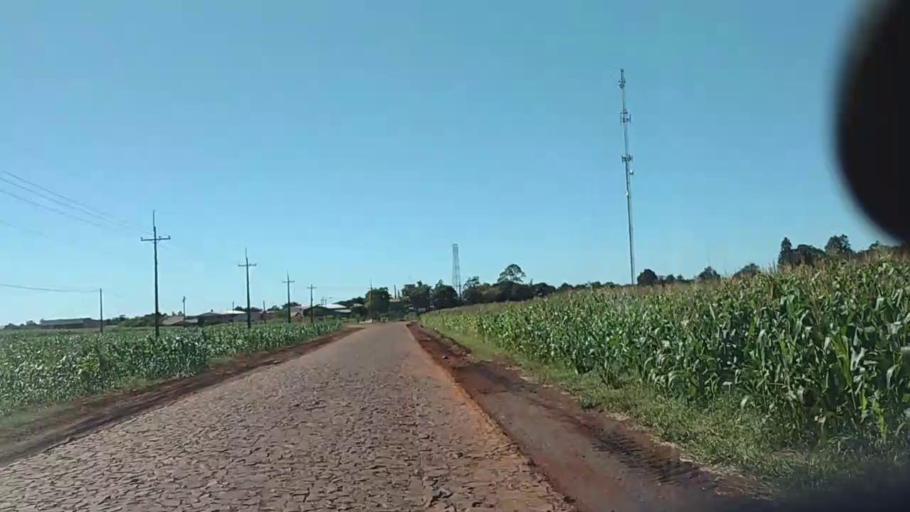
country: PY
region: Alto Parana
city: Naranjal
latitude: -25.9725
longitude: -55.2018
